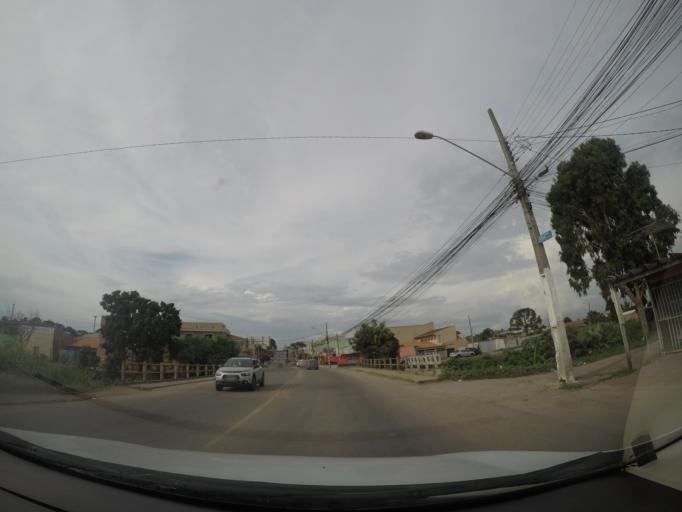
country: BR
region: Parana
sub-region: Sao Jose Dos Pinhais
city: Sao Jose dos Pinhais
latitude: -25.4915
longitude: -49.2298
